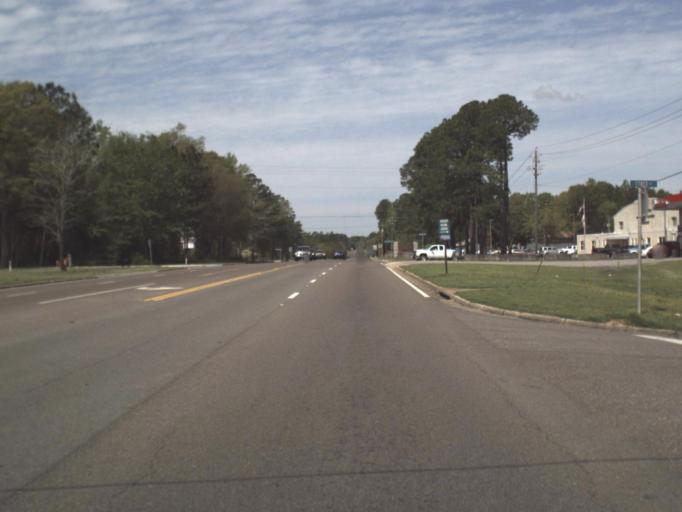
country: US
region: Florida
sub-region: Okaloosa County
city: Crestview
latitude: 30.7597
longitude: -86.5481
